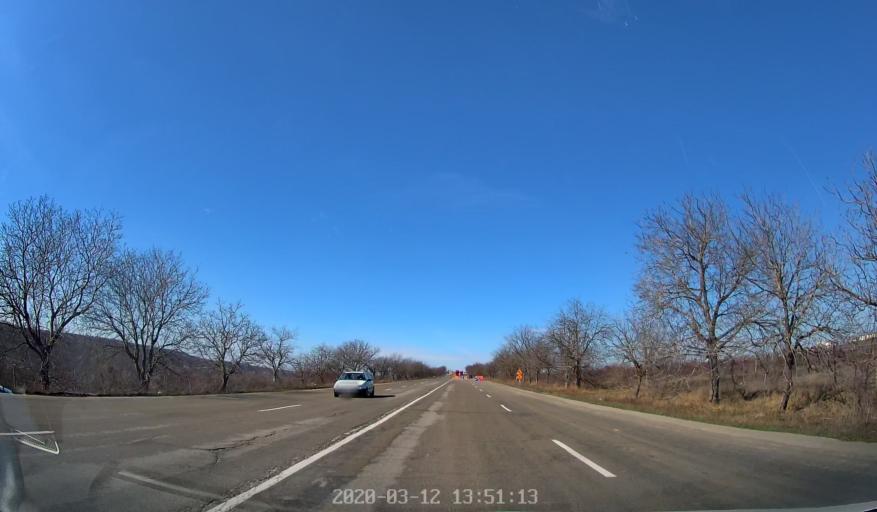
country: MD
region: Laloveni
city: Ialoveni
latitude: 46.9944
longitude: 28.7374
